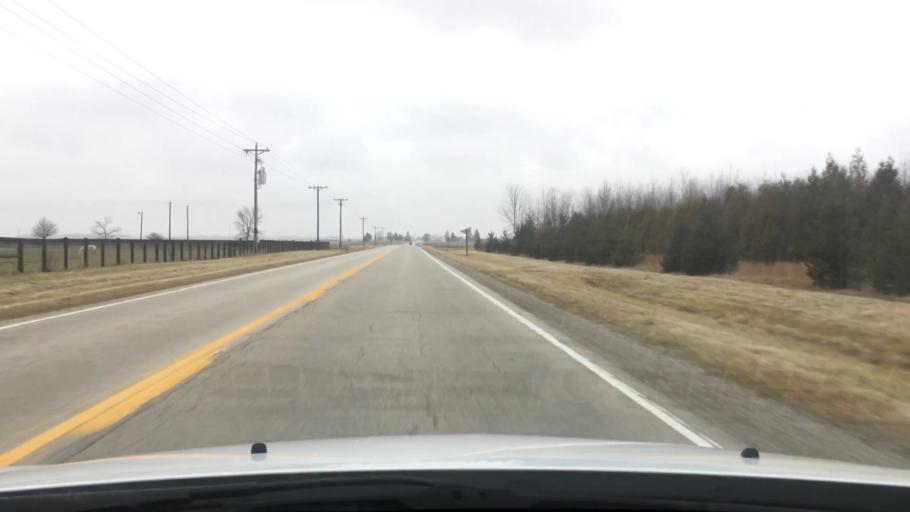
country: US
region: Illinois
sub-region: Iroquois County
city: Watseka
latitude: 40.8906
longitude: -87.6900
